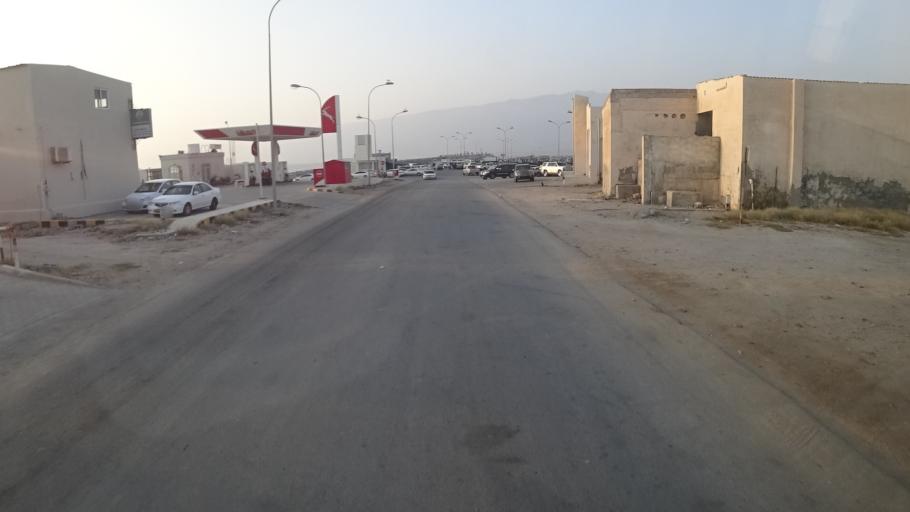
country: OM
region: Zufar
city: Salalah
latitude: 16.9850
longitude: 54.6871
